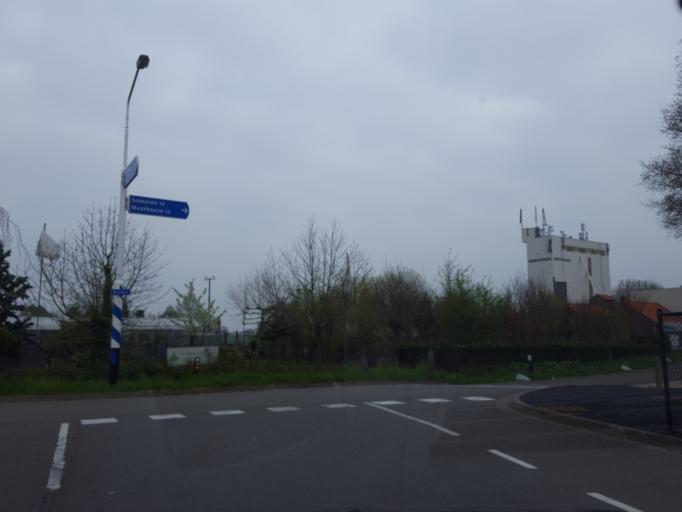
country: NL
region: Limburg
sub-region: Gemeente Nederweert
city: Nederweert
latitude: 51.2879
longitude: 5.7339
